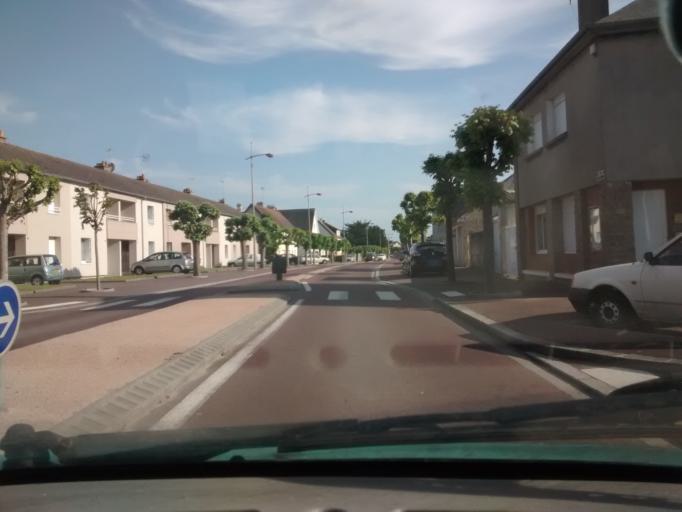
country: FR
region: Lower Normandy
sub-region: Departement de la Manche
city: Lessay
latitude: 49.2198
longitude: -1.5315
